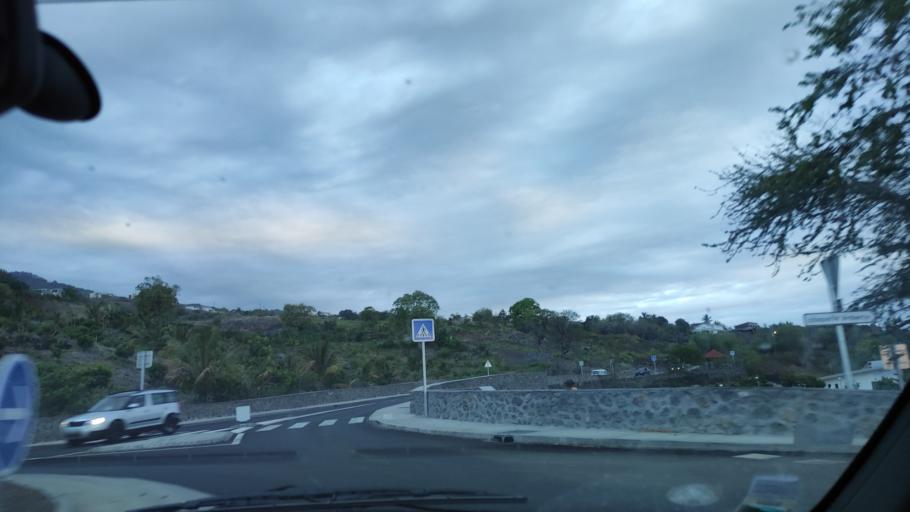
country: RE
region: Reunion
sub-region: Reunion
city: Saint-Leu
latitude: -21.1924
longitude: 55.2905
